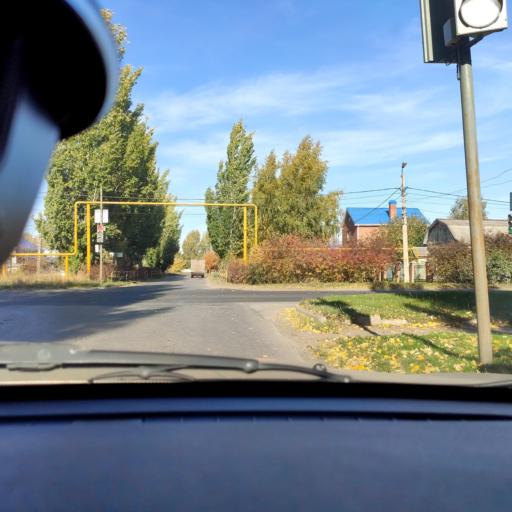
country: RU
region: Samara
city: Tol'yatti
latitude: 53.5382
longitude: 49.4164
